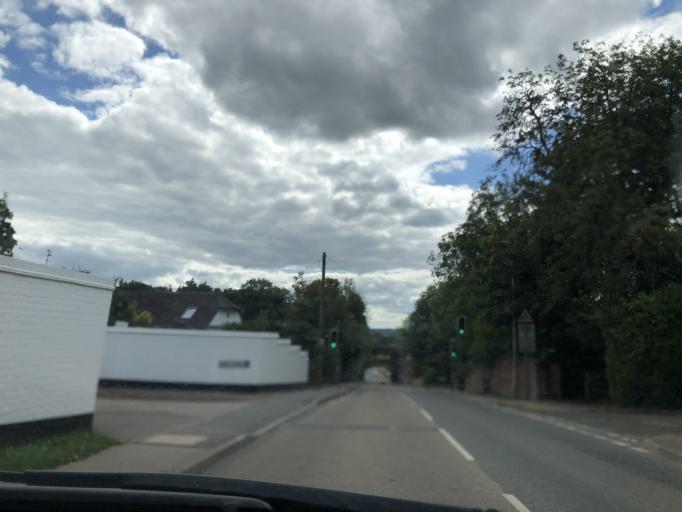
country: GB
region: England
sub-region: Kent
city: Edenbridge
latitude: 51.2098
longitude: 0.0607
